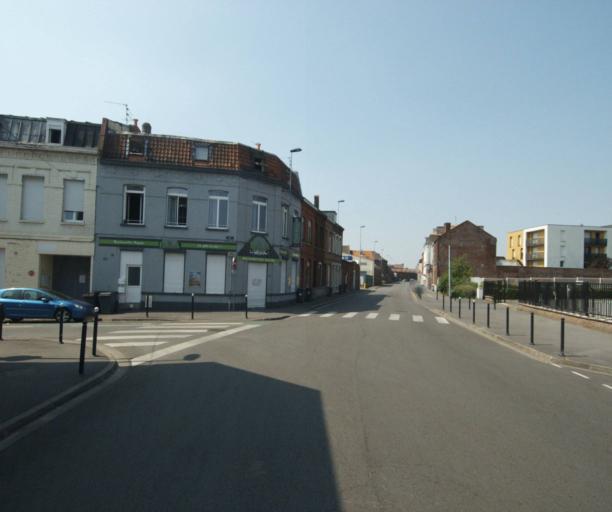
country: FR
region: Nord-Pas-de-Calais
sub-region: Departement du Nord
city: Tourcoing
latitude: 50.7175
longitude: 3.1525
